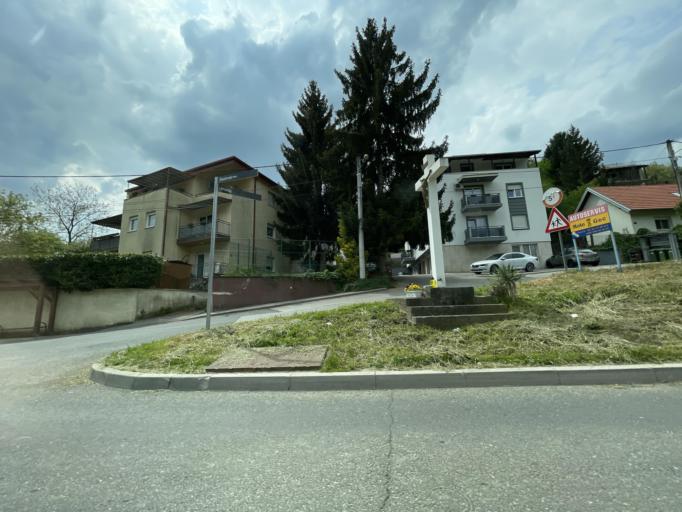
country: HR
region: Grad Zagreb
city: Zagreb
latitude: 45.8323
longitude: 15.9453
